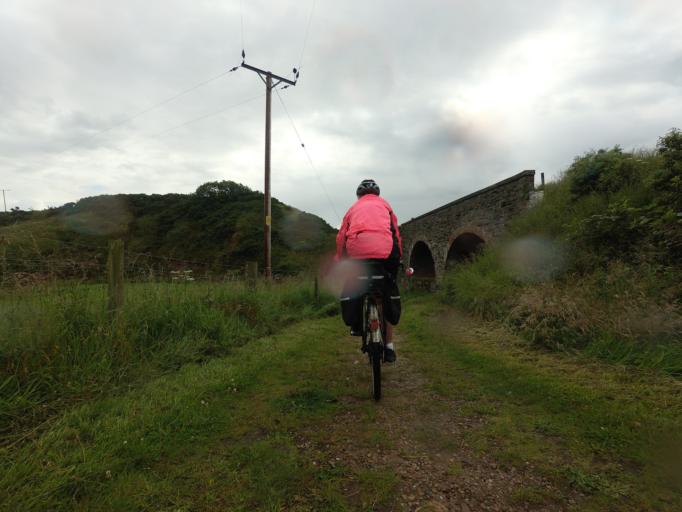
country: GB
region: Scotland
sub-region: Moray
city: Buckie
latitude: 57.6685
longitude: -2.9979
